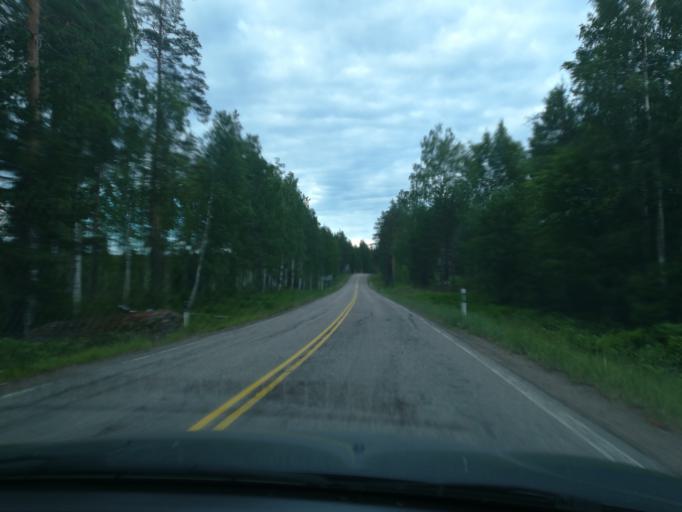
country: FI
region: South Karelia
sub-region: Lappeenranta
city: Savitaipale
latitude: 61.4990
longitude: 27.8315
